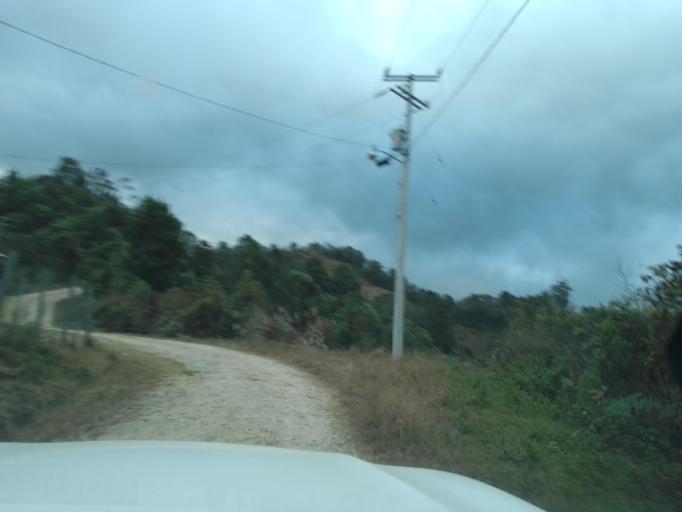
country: MX
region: Chiapas
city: Motozintla de Mendoza
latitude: 15.2122
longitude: -92.2275
